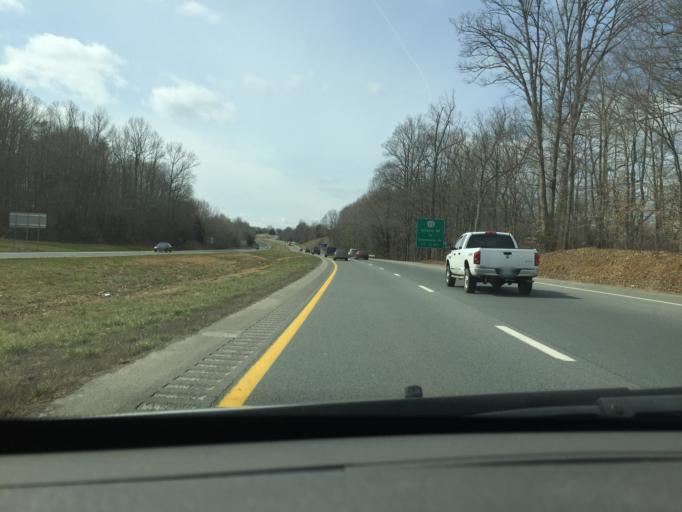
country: US
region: Virginia
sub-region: Campbell County
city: Timberlake
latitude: 37.3391
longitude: -79.1985
